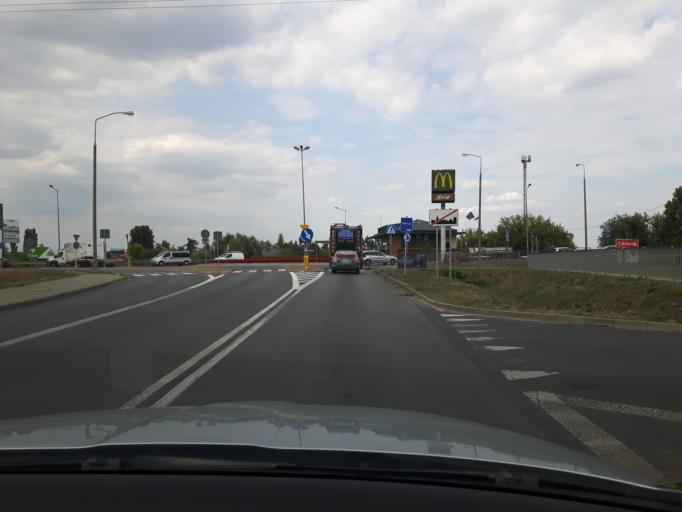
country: PL
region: Masovian Voivodeship
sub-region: Powiat legionowski
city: Nieporet
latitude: 52.4320
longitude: 21.0310
